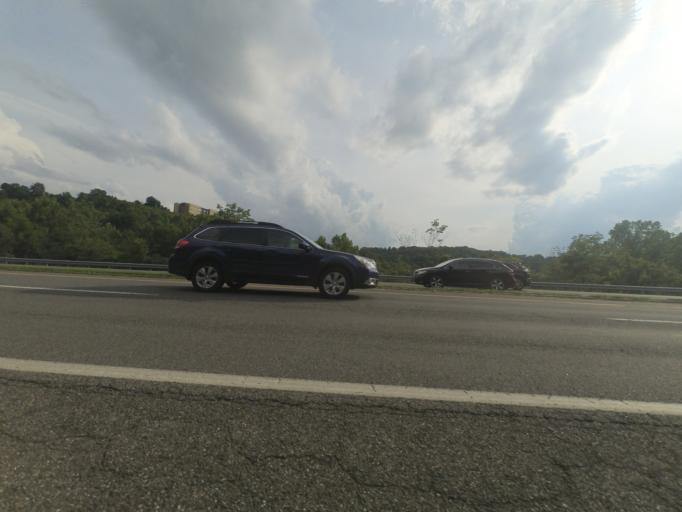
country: US
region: West Virginia
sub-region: Cabell County
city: Huntington
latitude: 38.3985
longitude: -82.4217
